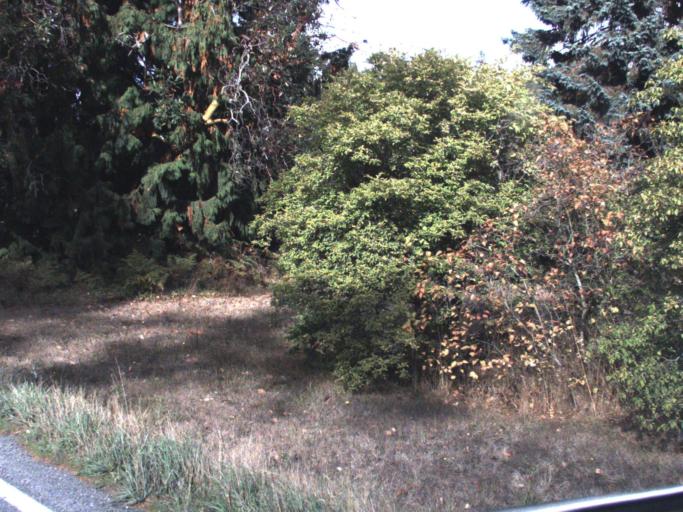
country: US
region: Washington
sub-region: Island County
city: Coupeville
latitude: 48.1781
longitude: -122.6189
